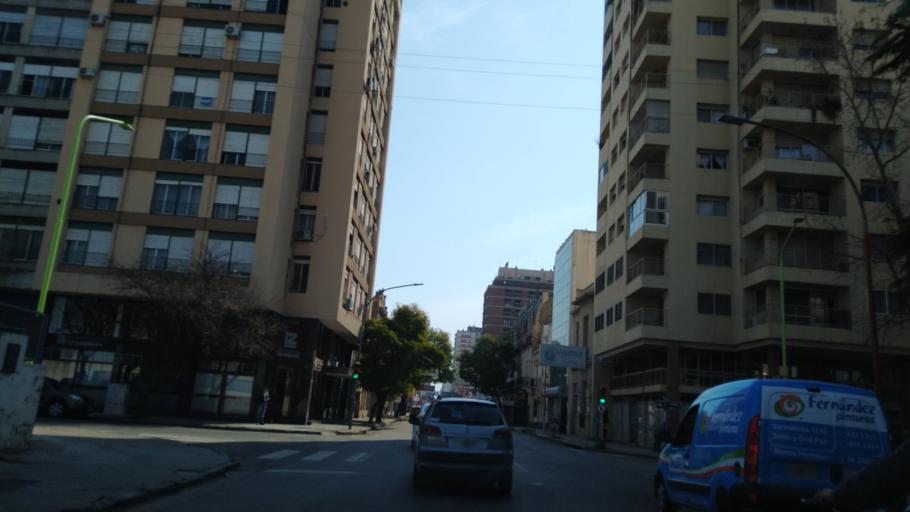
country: AR
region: Buenos Aires
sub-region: Partido de Bahia Blanca
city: Bahia Blanca
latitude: -38.7243
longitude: -62.2626
